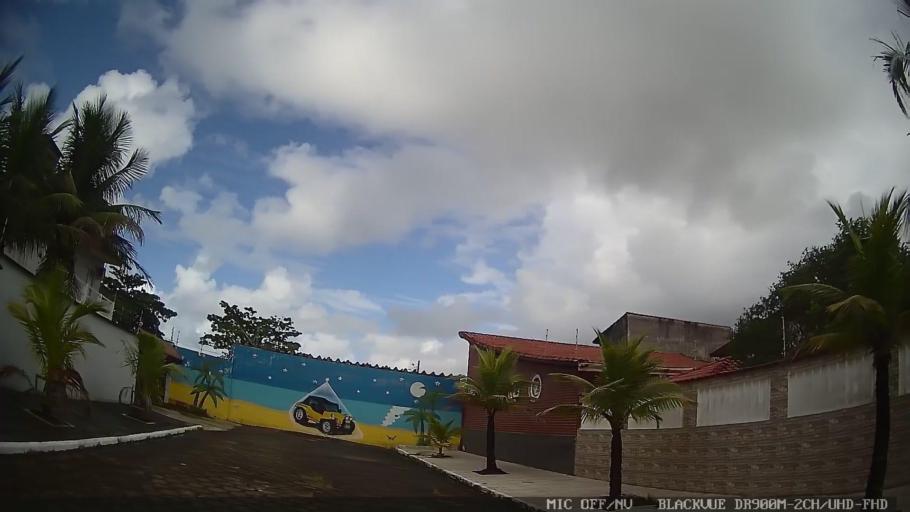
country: BR
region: Sao Paulo
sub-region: Itanhaem
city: Itanhaem
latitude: -24.2314
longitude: -46.8711
